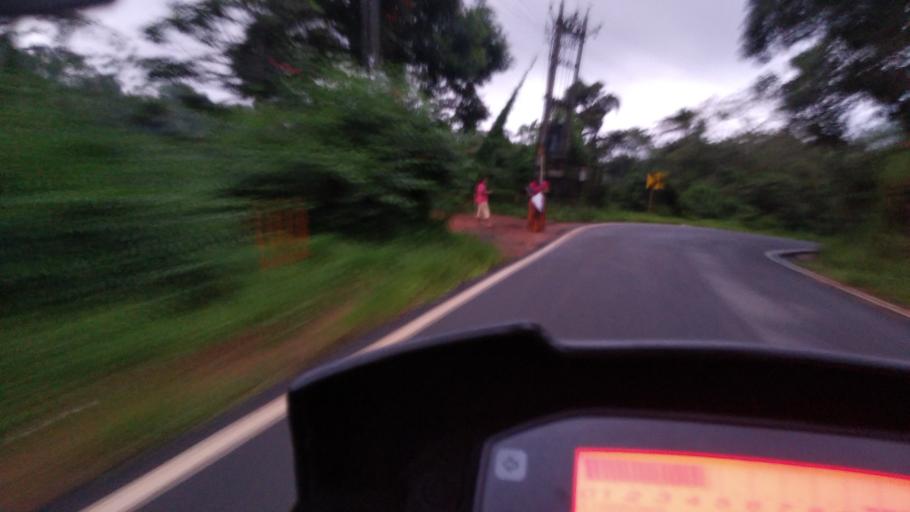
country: IN
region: Kerala
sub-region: Idukki
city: Munnar
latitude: 9.9557
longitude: 77.0837
